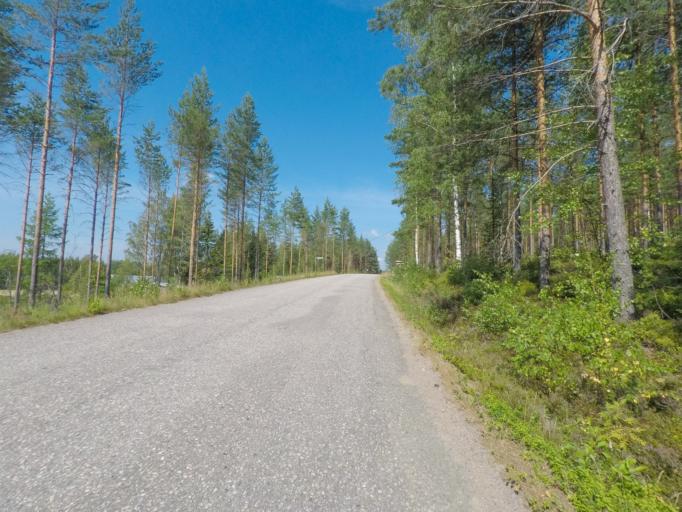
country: FI
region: Southern Savonia
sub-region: Mikkeli
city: Puumala
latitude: 61.4162
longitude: 28.0922
